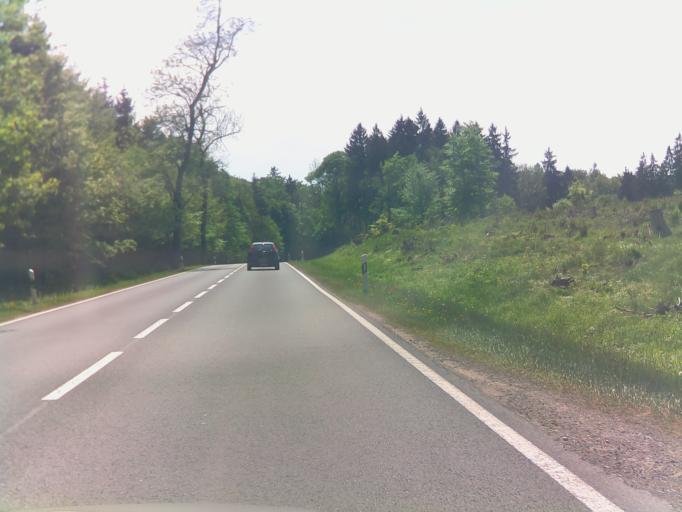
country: DE
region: Saxony-Anhalt
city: Hasselfelde
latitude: 51.7167
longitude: 10.8941
